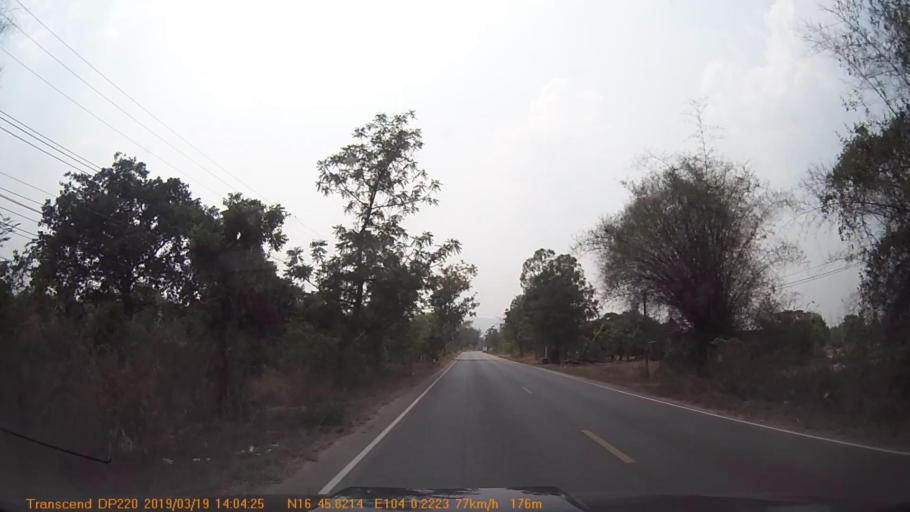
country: TH
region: Kalasin
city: Na Khu
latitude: 16.7638
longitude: 104.0032
